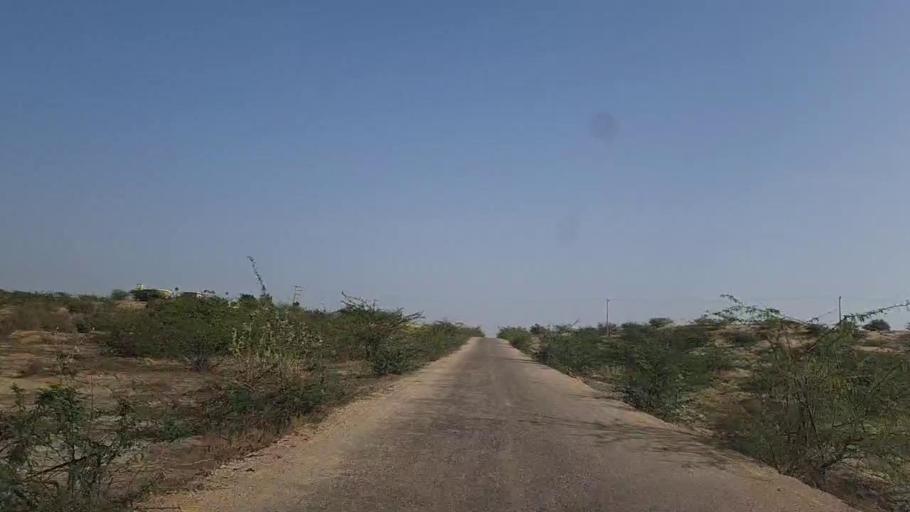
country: PK
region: Sindh
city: Naukot
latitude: 24.6251
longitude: 69.3676
